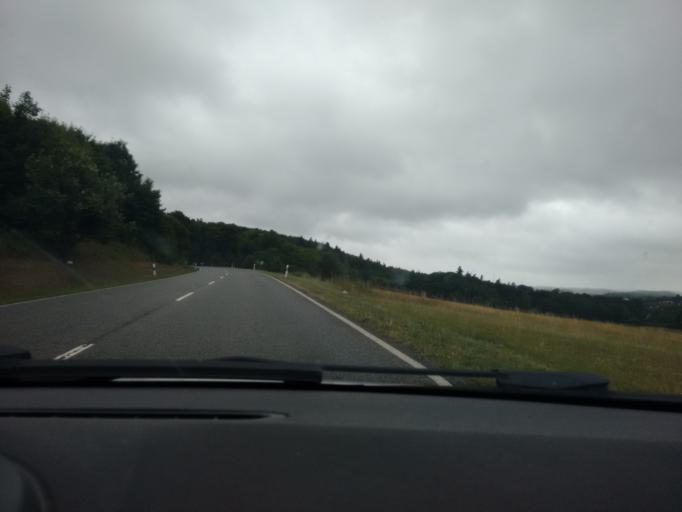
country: DE
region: Rheinland-Pfalz
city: Schmissberg
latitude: 49.6611
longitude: 7.1910
